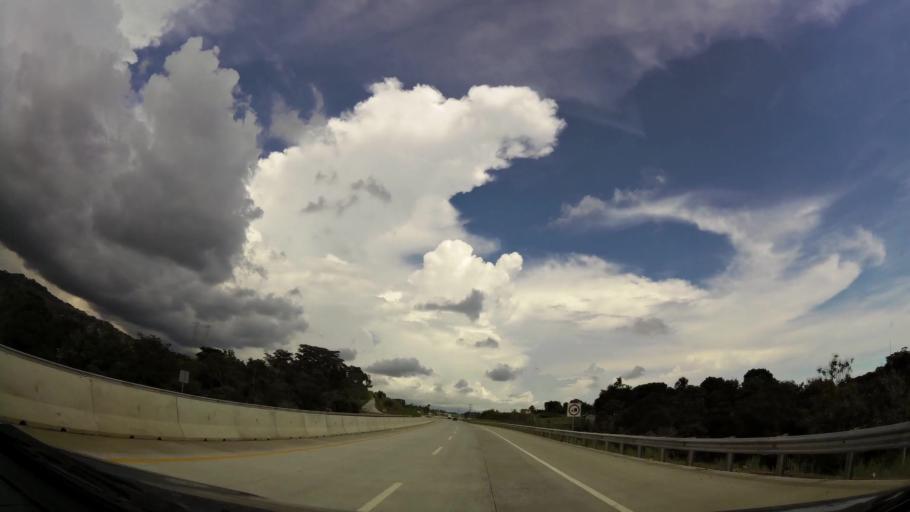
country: PA
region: Panama
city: San Miguelito
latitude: 9.0901
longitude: -79.4370
